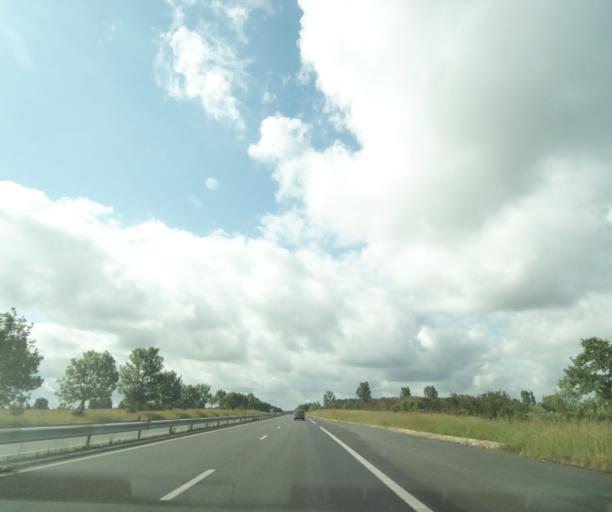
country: FR
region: Pays de la Loire
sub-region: Departement de Maine-et-Loire
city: Durtal
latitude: 47.7170
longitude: -0.2512
